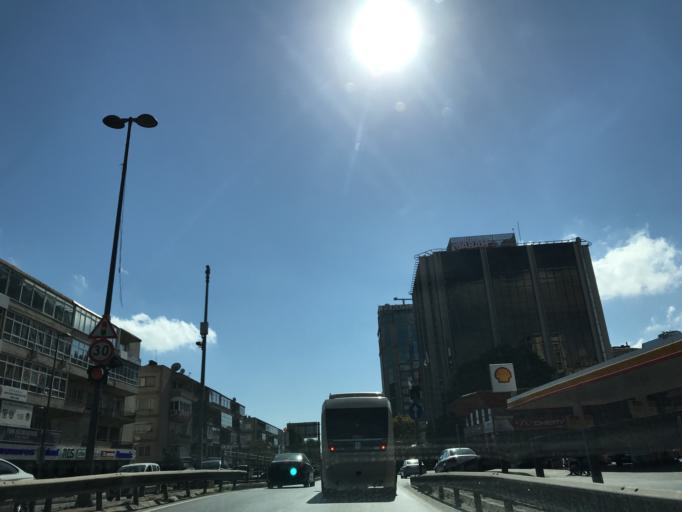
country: TR
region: Istanbul
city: Sisli
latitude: 41.0617
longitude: 29.0113
